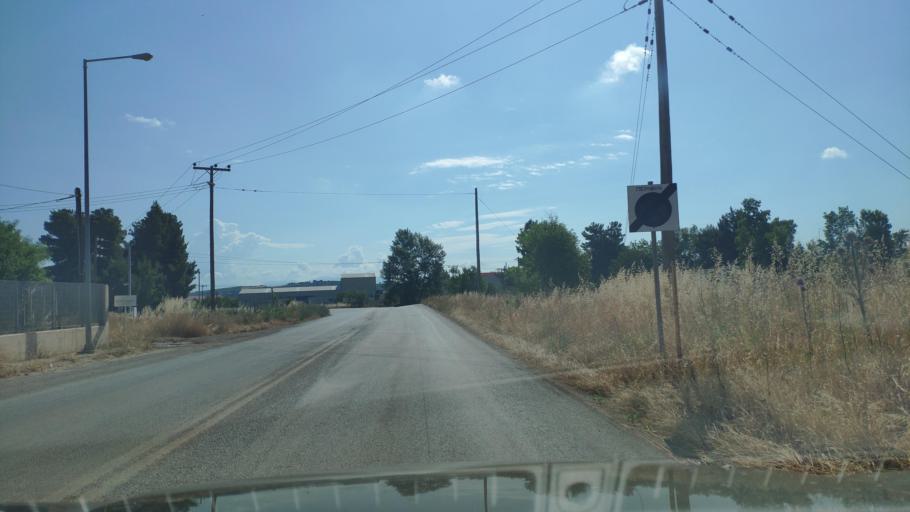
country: GR
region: Central Greece
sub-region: Nomos Voiotias
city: Arma
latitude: 38.3811
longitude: 23.4943
